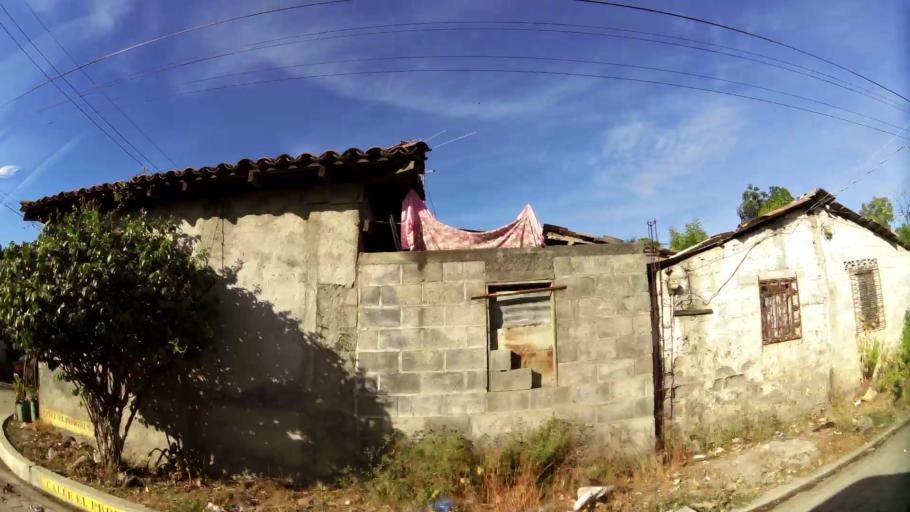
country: SV
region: San Miguel
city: San Miguel
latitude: 13.4630
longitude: -88.1866
